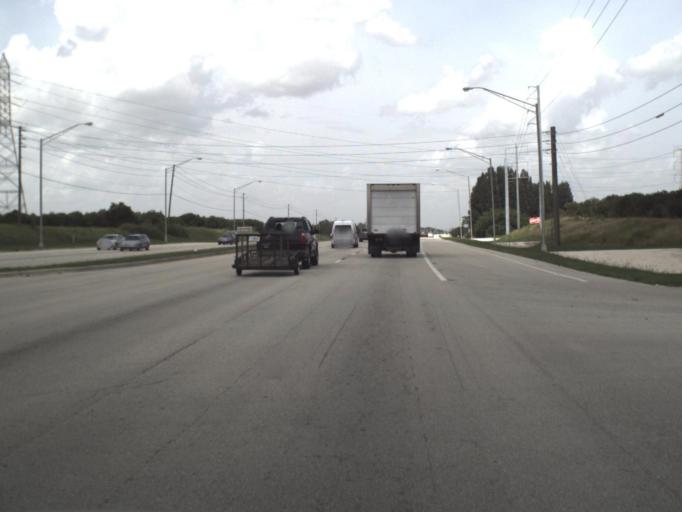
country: US
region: Florida
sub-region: Highlands County
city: Avon Park
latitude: 27.5699
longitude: -81.5142
